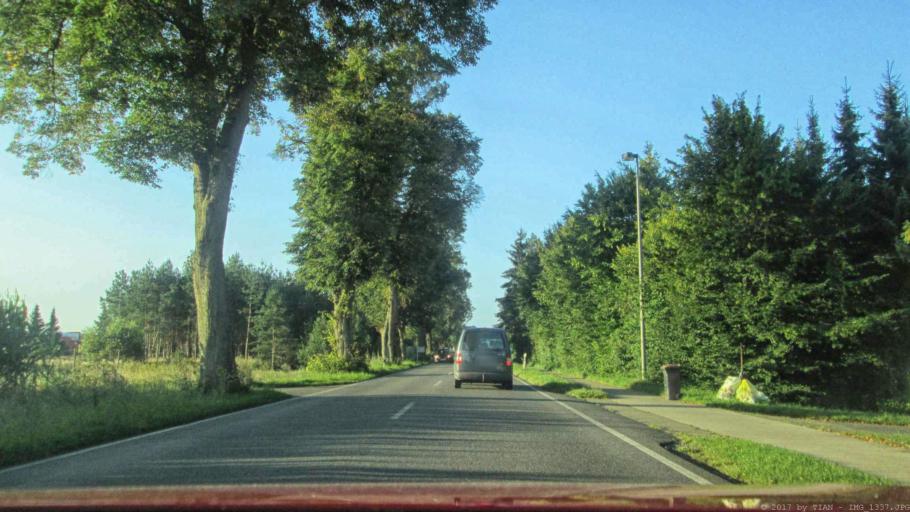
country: DE
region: Lower Saxony
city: Bodenteich
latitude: 52.8430
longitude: 10.6821
